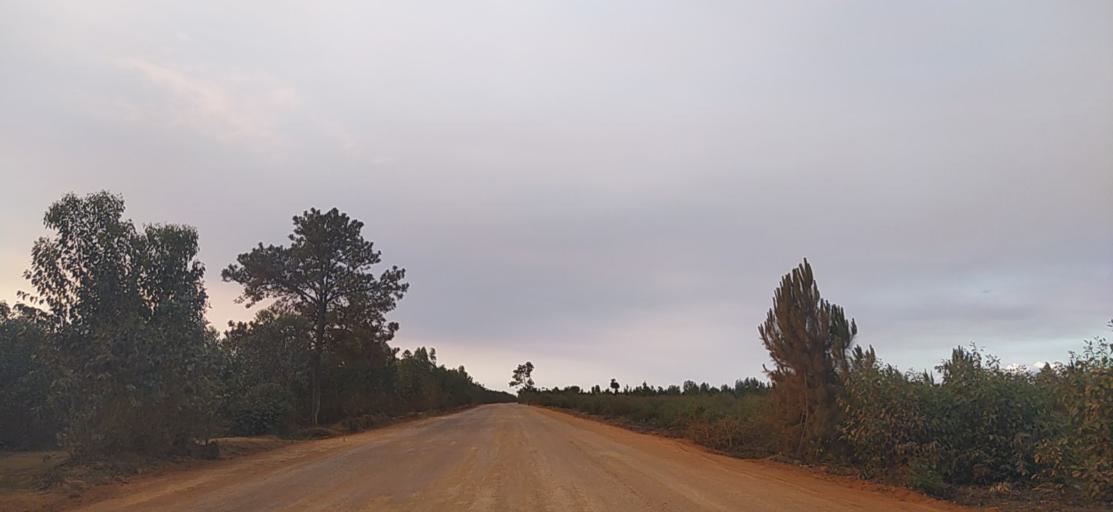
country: MG
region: Analamanga
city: Anjozorobe
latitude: -18.4722
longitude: 48.2618
